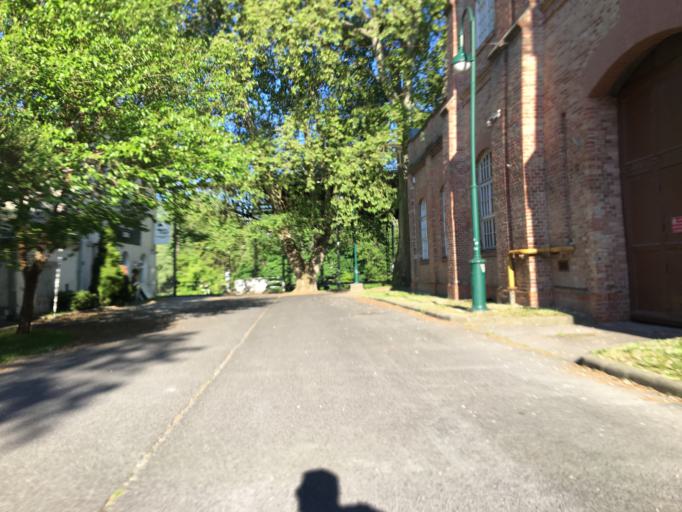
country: HU
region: Budapest
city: Budapest III. keruelet
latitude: 47.5417
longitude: 19.0489
